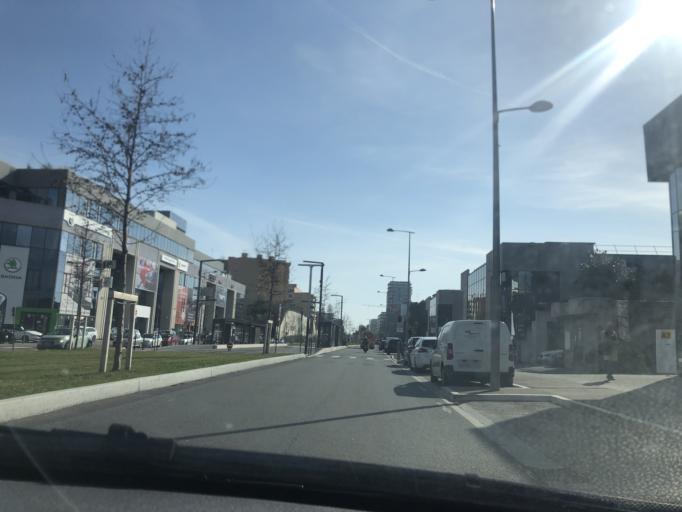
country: FR
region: Provence-Alpes-Cote d'Azur
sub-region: Departement des Alpes-Maritimes
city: Saint-Laurent-du-Var
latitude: 43.6882
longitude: 7.2013
